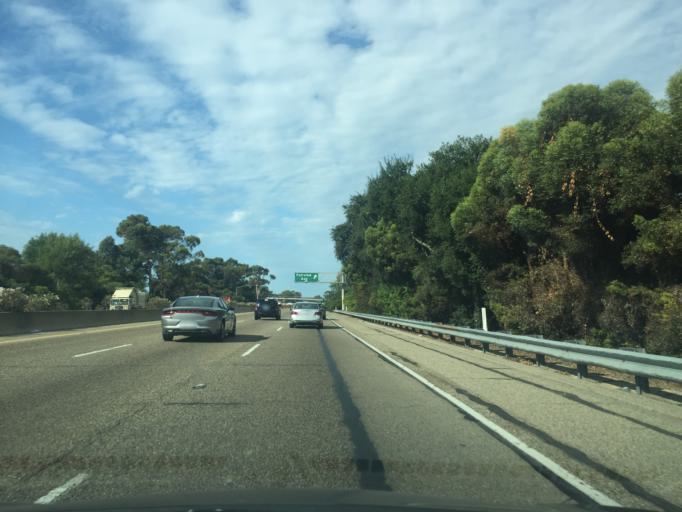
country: US
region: California
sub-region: Santa Barbara County
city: Goleta
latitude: 34.4404
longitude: -119.8243
